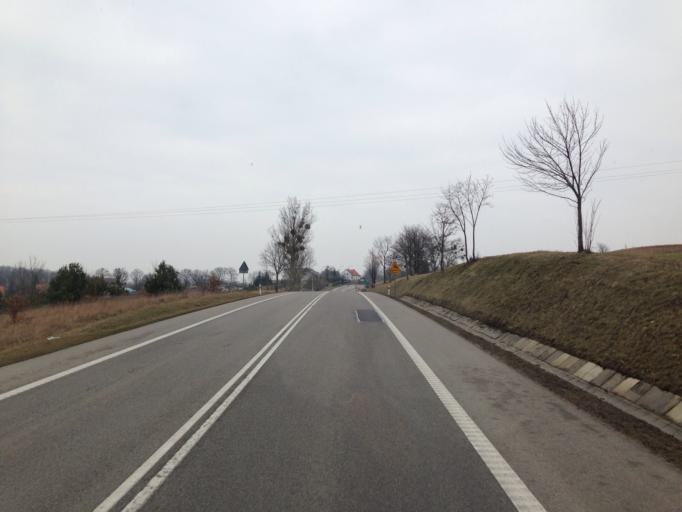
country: PL
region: Pomeranian Voivodeship
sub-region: Powiat starogardzki
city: Smetowo Graniczne
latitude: 53.7627
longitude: 18.7665
